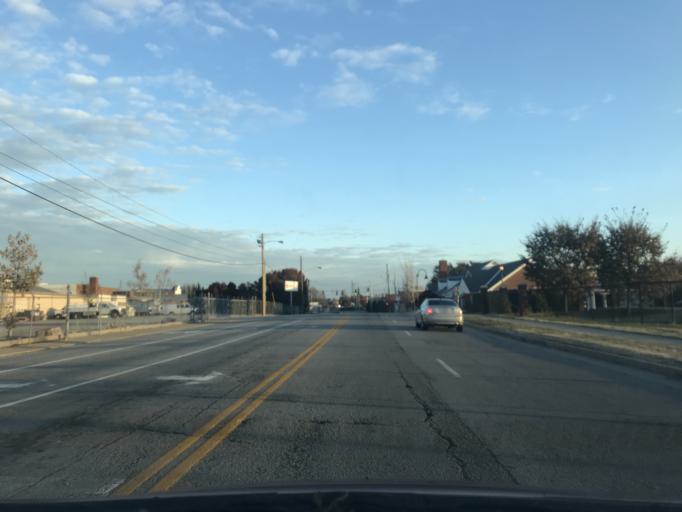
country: US
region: Indiana
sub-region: Clark County
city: Jeffersonville
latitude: 38.2514
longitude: -85.7329
